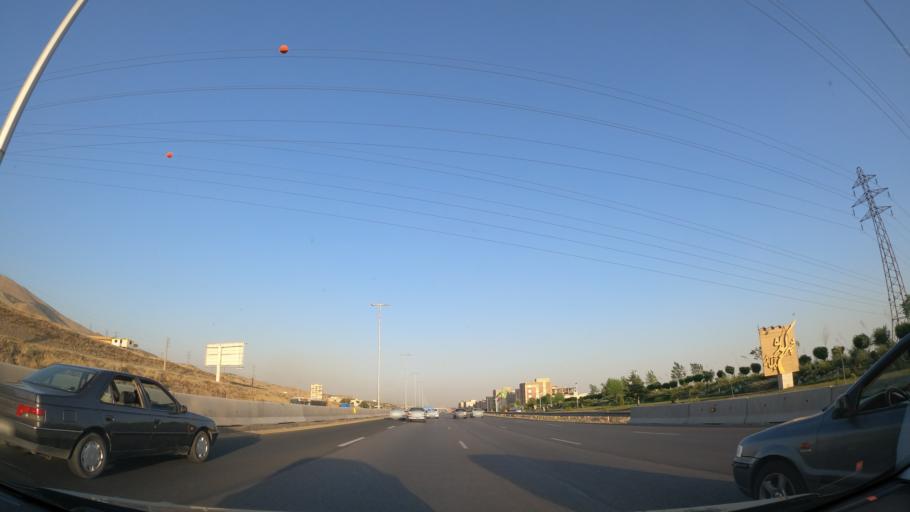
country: IR
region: Tehran
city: Shahr-e Qods
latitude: 35.7605
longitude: 51.0642
